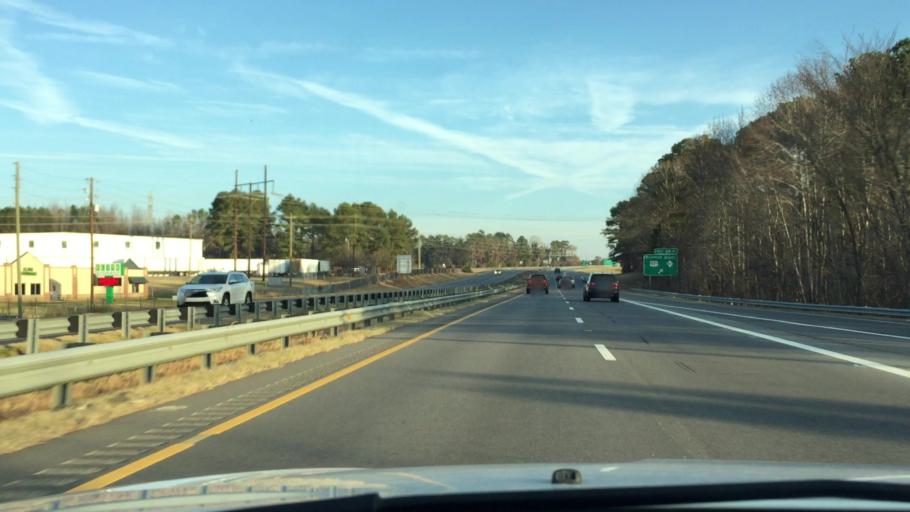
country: US
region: North Carolina
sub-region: Lee County
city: Sanford
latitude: 35.4895
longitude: -79.1968
